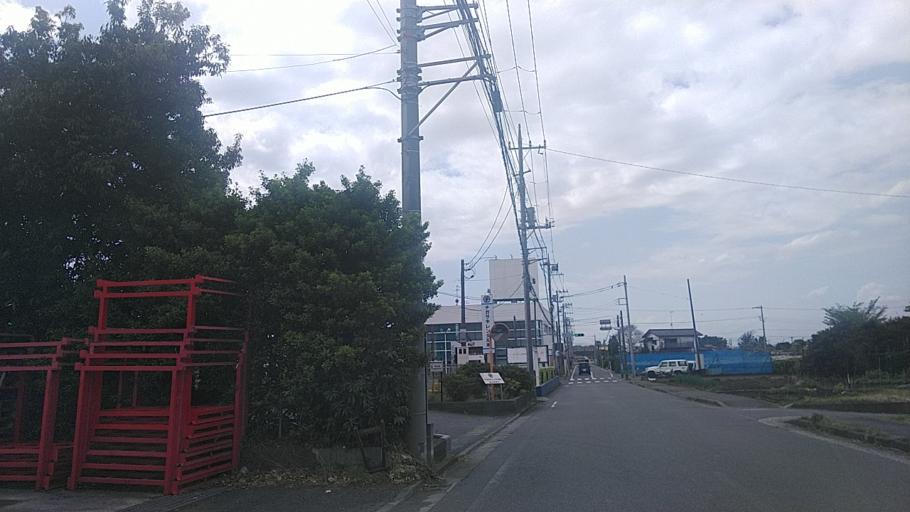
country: JP
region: Kanagawa
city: Fujisawa
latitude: 35.3831
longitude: 139.4434
